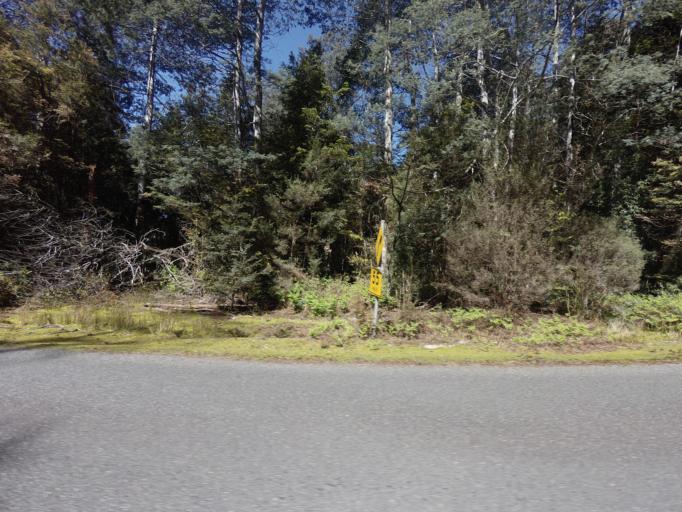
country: AU
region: Tasmania
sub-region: Huon Valley
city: Geeveston
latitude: -42.8155
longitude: 146.3679
